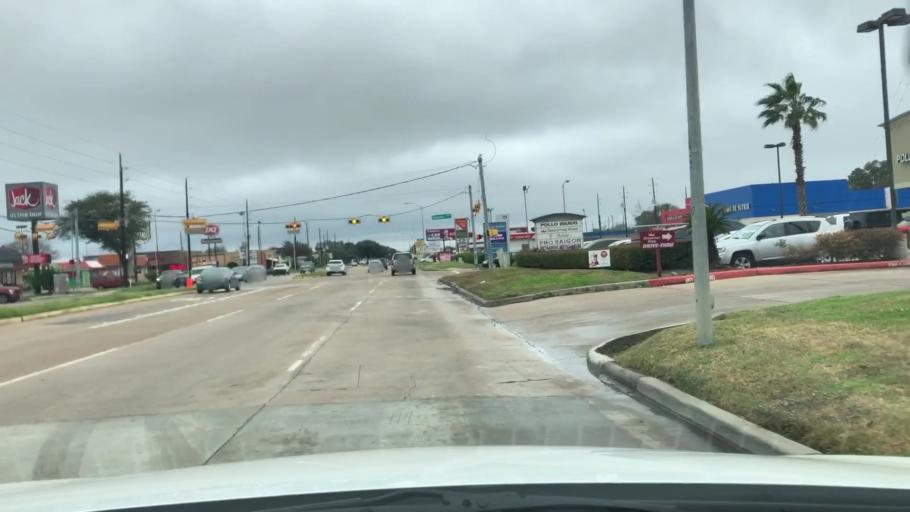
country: US
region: Texas
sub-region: Fort Bend County
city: Cinco Ranch
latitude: 29.7702
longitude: -95.7518
